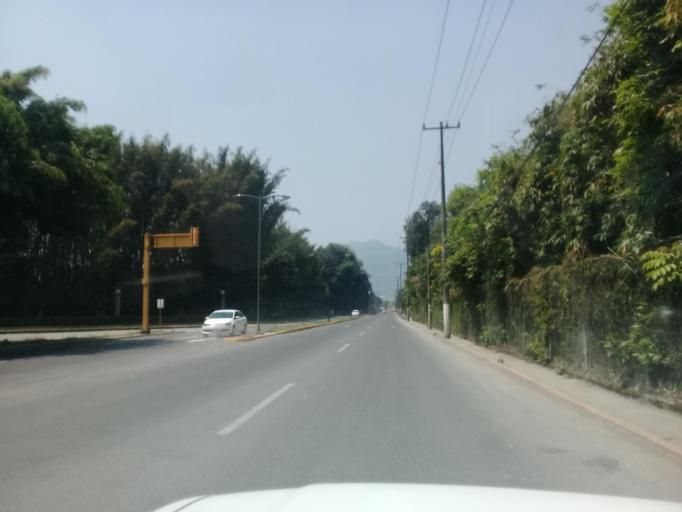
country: MX
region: Veracruz
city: Ixtac Zoquitlan
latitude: 18.8617
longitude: -97.0429
